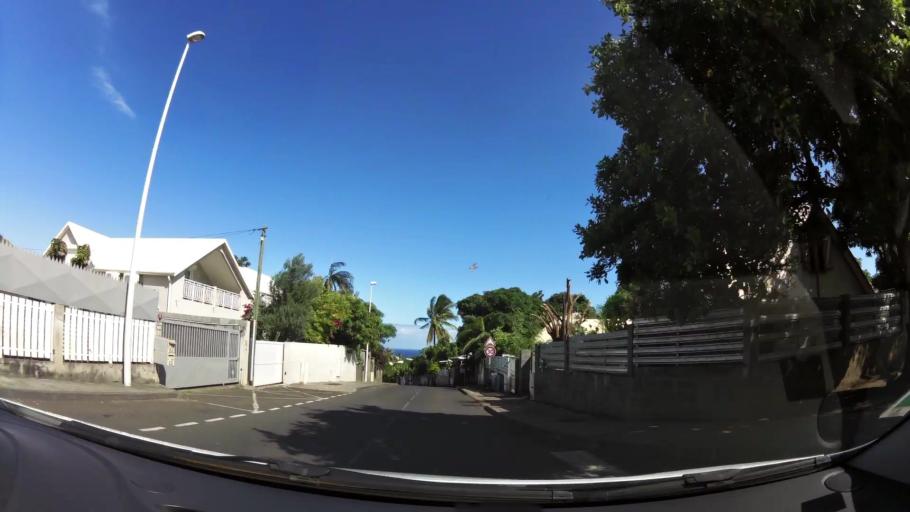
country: RE
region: Reunion
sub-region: Reunion
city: Saint-Pierre
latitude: -21.3238
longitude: 55.4810
